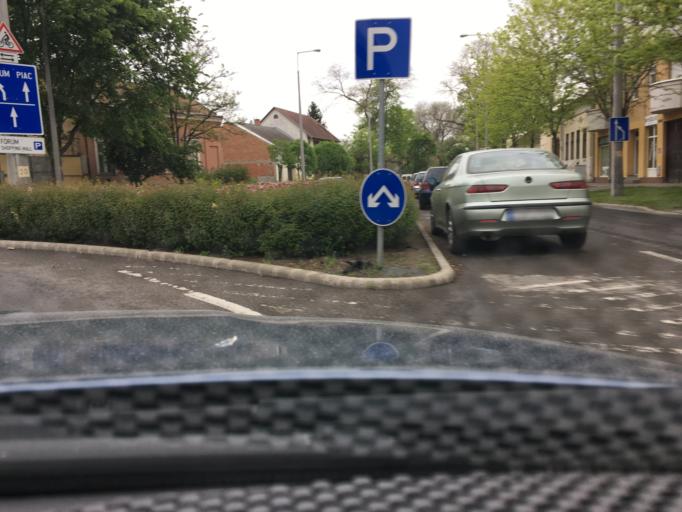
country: HU
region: Hajdu-Bihar
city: Debrecen
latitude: 47.5346
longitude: 21.6286
